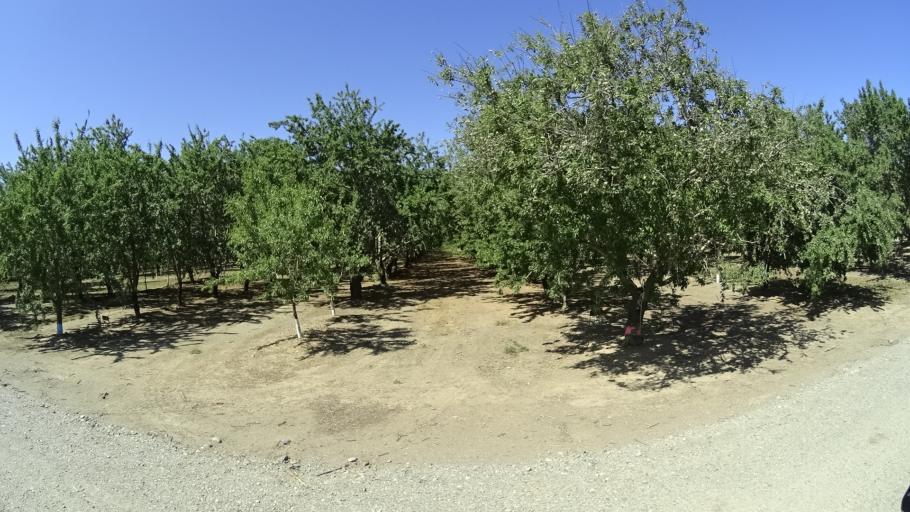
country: US
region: California
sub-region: Glenn County
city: Orland
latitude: 39.6851
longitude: -122.1592
